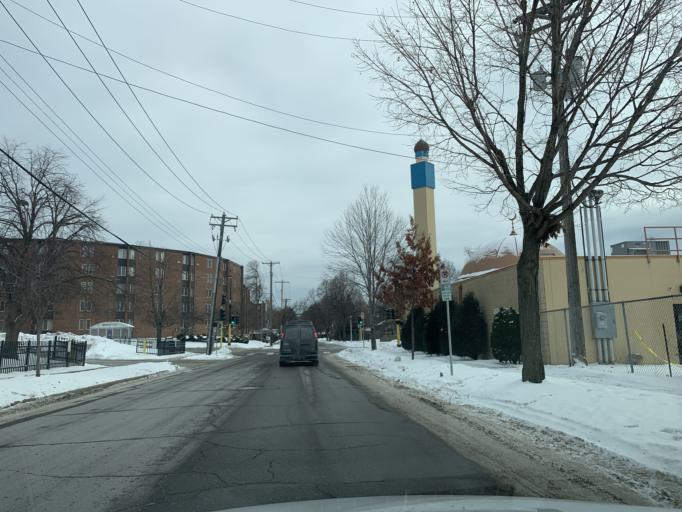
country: US
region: Minnesota
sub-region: Hennepin County
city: Minneapolis
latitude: 44.9974
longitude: -93.2888
